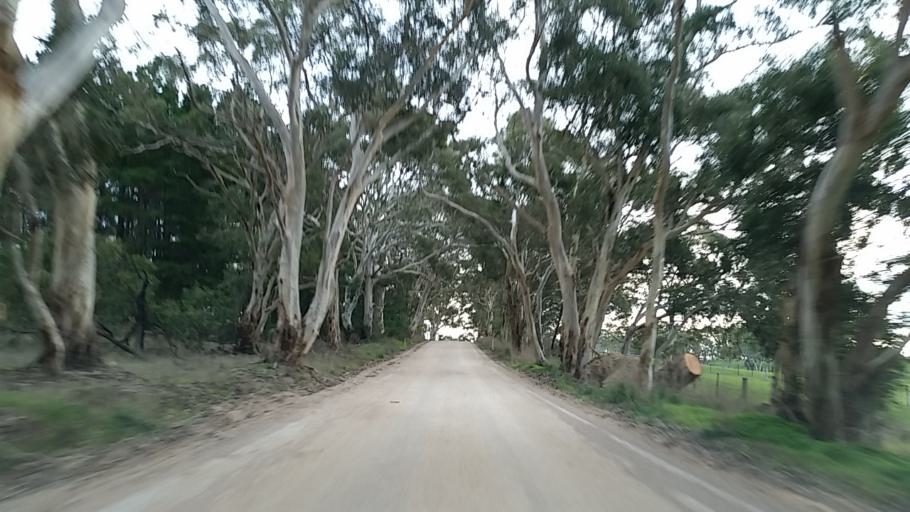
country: AU
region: South Australia
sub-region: Adelaide Hills
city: Birdwood
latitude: -34.8778
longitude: 138.9775
